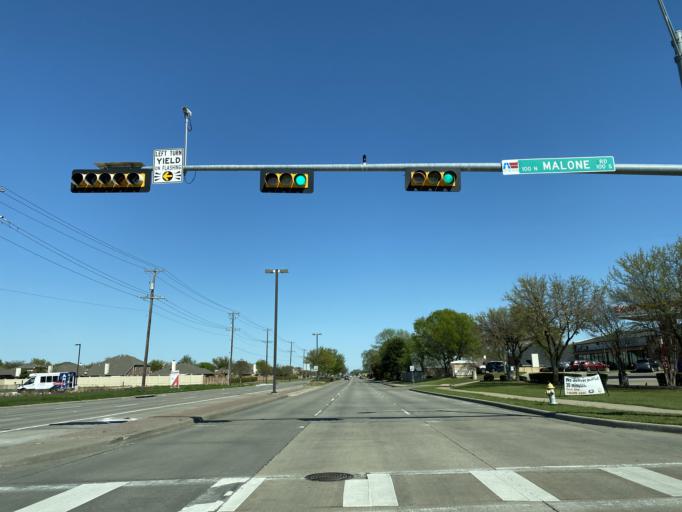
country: US
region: Texas
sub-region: Collin County
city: Allen
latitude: 33.1002
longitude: -96.6288
